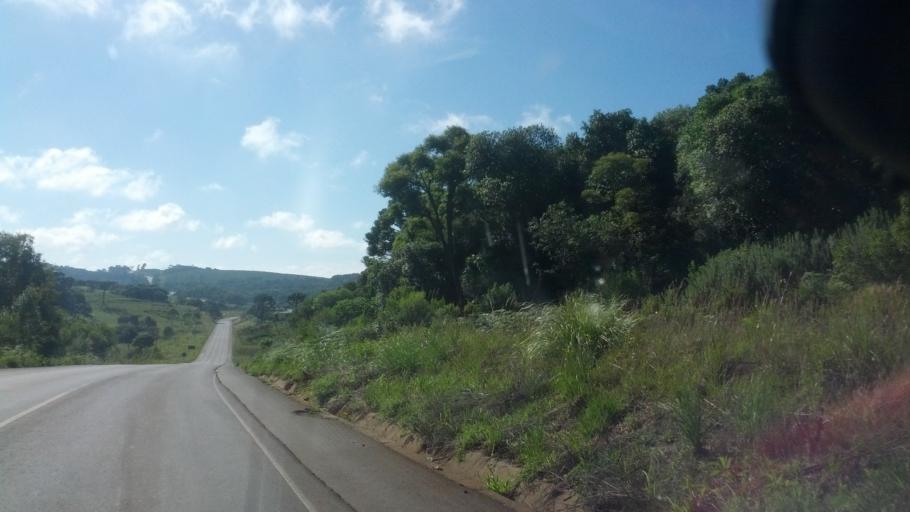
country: BR
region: Rio Grande do Sul
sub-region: Vacaria
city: Estrela
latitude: -27.9024
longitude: -50.7321
